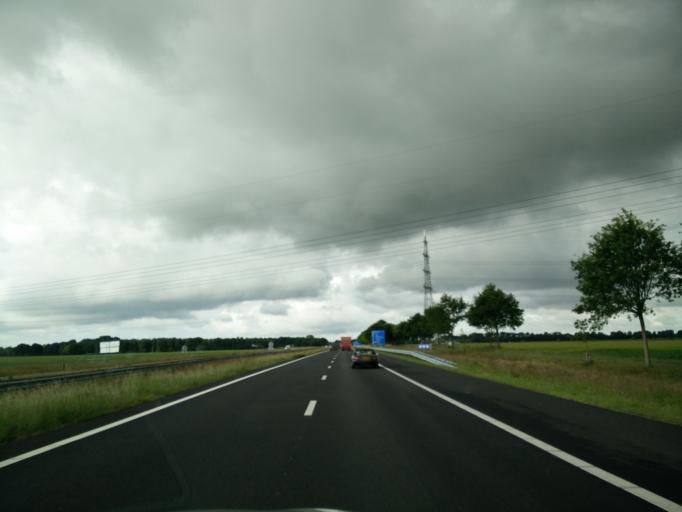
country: NL
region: Drenthe
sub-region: Gemeente Assen
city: Assen
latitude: 52.8850
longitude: 6.5222
